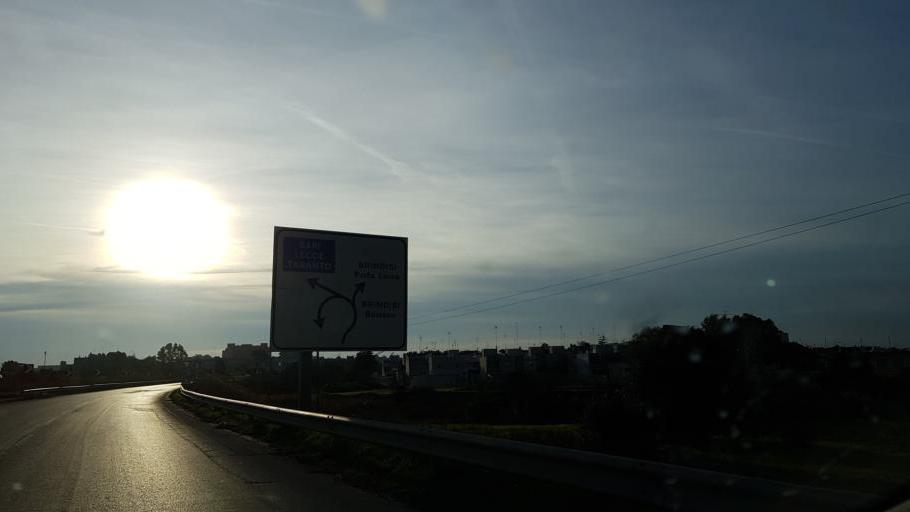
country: IT
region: Apulia
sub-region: Provincia di Brindisi
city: La Rosa
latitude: 40.6271
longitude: 17.9595
